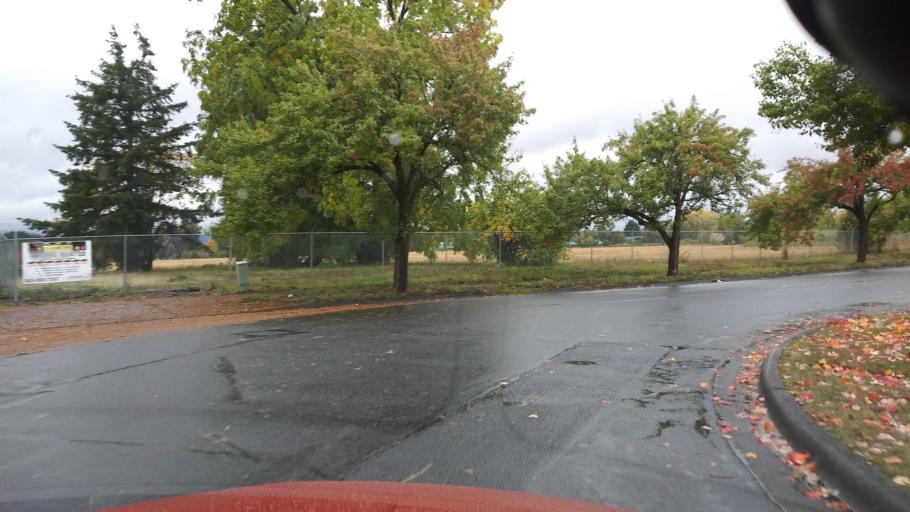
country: US
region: Oregon
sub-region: Washington County
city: Cornelius
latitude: 45.5141
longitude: -123.0756
